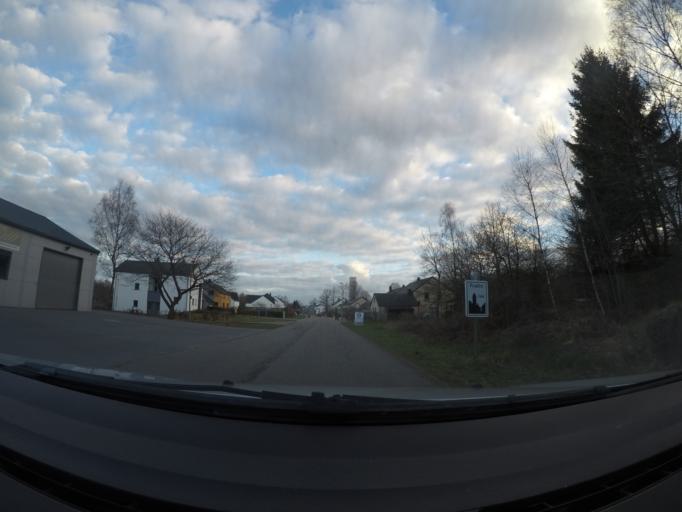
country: BE
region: Wallonia
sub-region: Province du Luxembourg
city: Etalle
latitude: 49.6649
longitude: 5.5705
